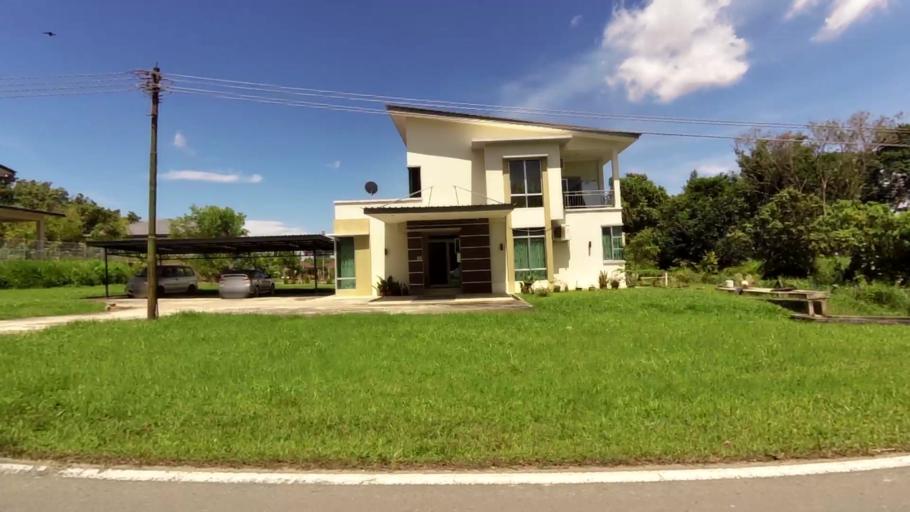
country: BN
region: Brunei and Muara
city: Bandar Seri Begawan
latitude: 4.9358
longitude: 114.9505
